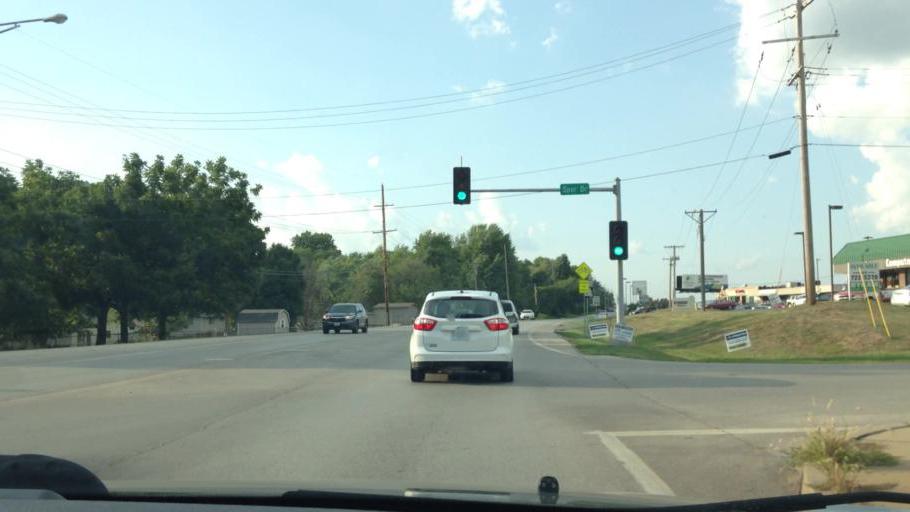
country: US
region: Missouri
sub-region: Platte County
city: Weatherby Lake
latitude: 39.2339
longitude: -94.6584
